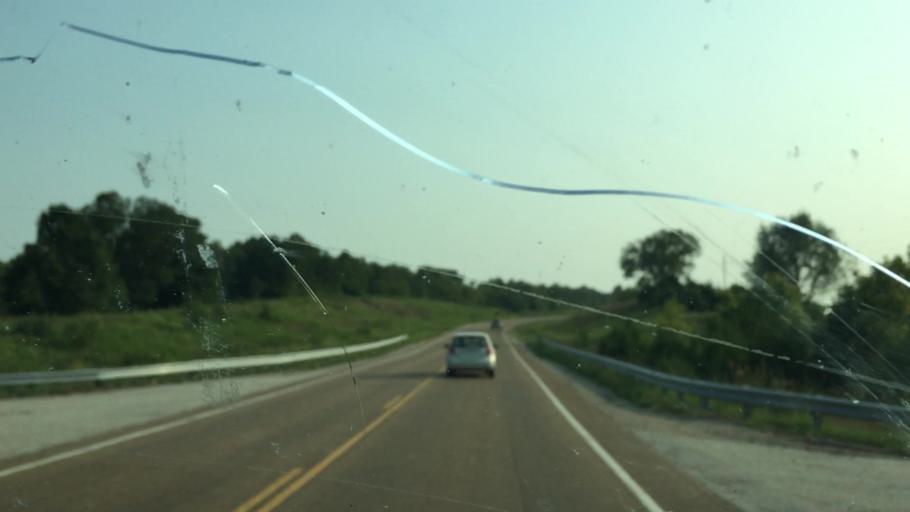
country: US
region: Missouri
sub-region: Pulaski County
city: Richland
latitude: 37.7941
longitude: -92.4067
